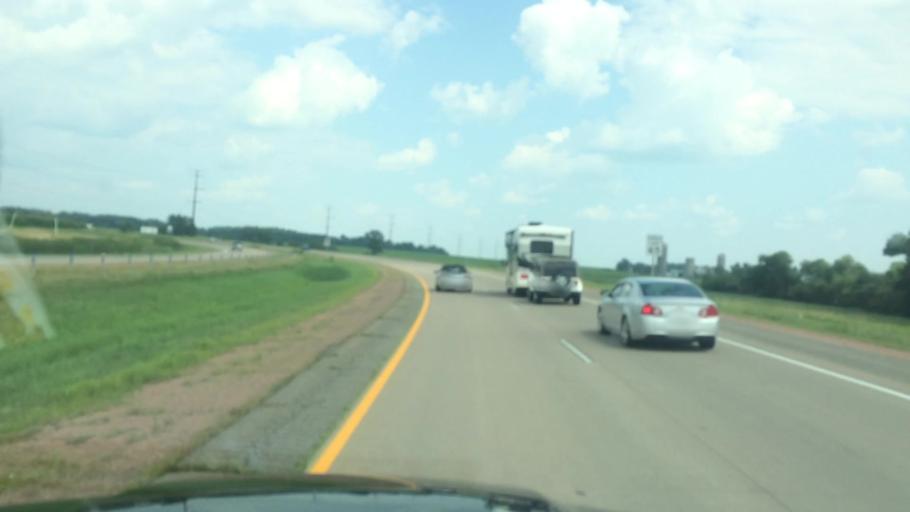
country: US
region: Wisconsin
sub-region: Clark County
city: Abbotsford
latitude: 44.9325
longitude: -90.3001
